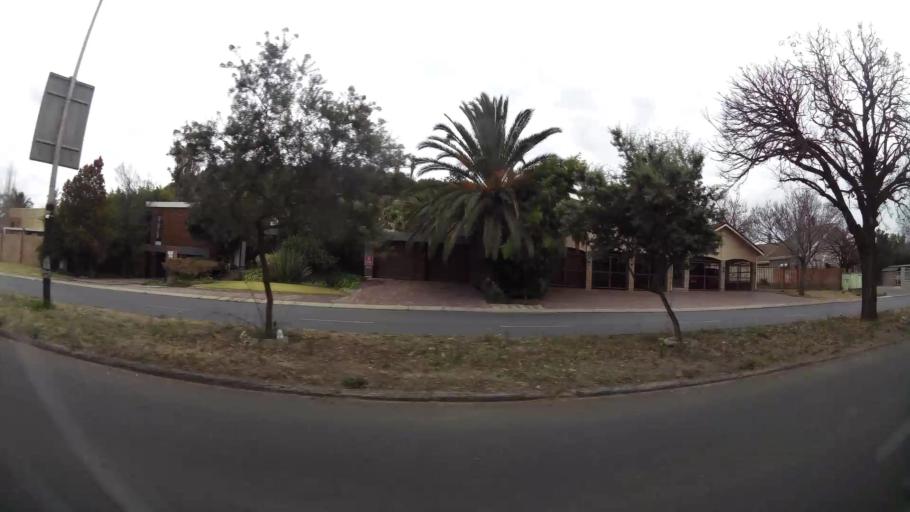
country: ZA
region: Orange Free State
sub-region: Mangaung Metropolitan Municipality
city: Bloemfontein
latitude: -29.0896
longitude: 26.2042
